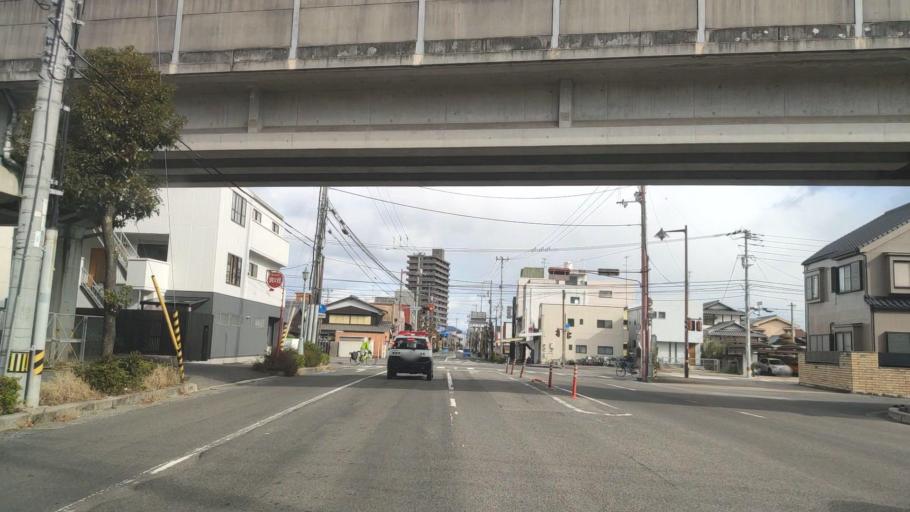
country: JP
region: Ehime
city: Hojo
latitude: 34.0667
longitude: 132.9911
